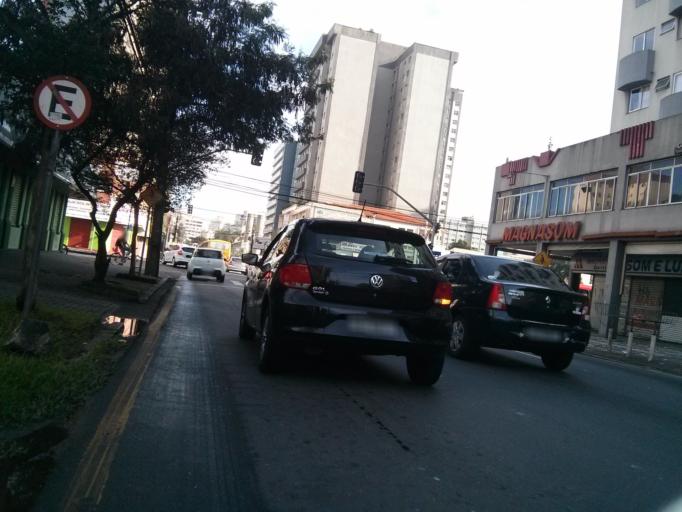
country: BR
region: Parana
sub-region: Curitiba
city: Curitiba
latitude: -25.4400
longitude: -49.2720
